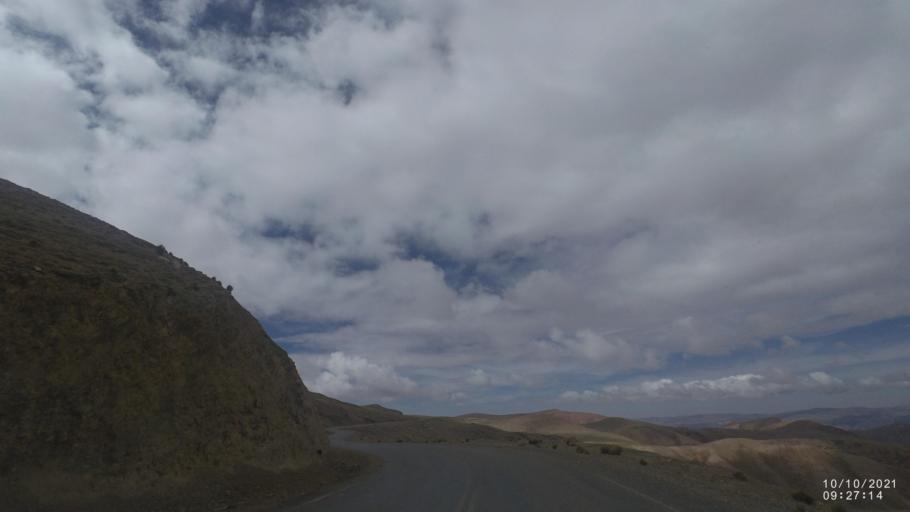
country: BO
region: La Paz
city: Quime
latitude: -17.0979
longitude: -67.3245
